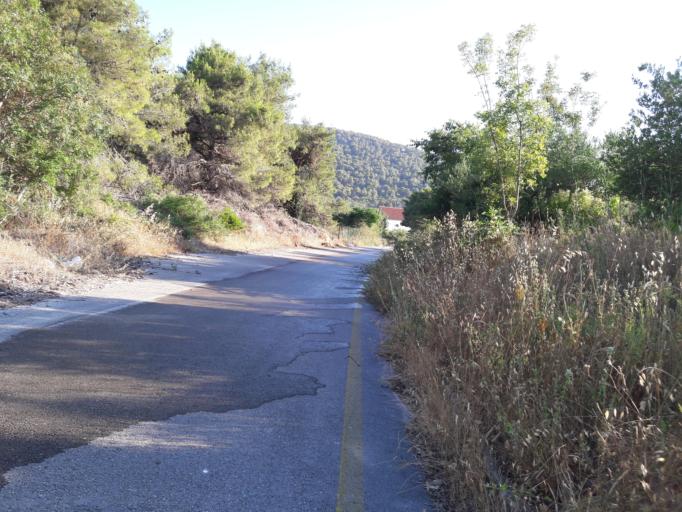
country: HR
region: Sibensko-Kniniska
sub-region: Grad Sibenik
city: Sibenik
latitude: 43.6957
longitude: 15.8460
